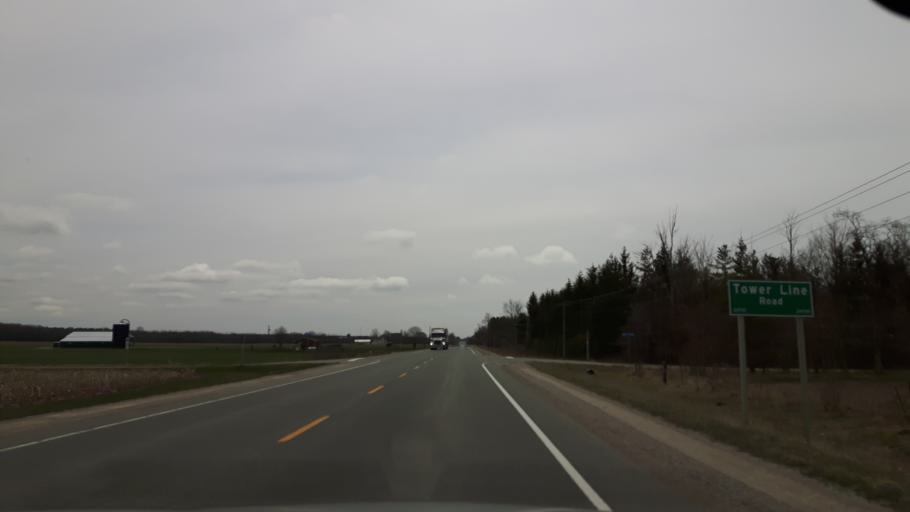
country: CA
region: Ontario
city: Goderich
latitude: 43.6246
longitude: -81.7059
